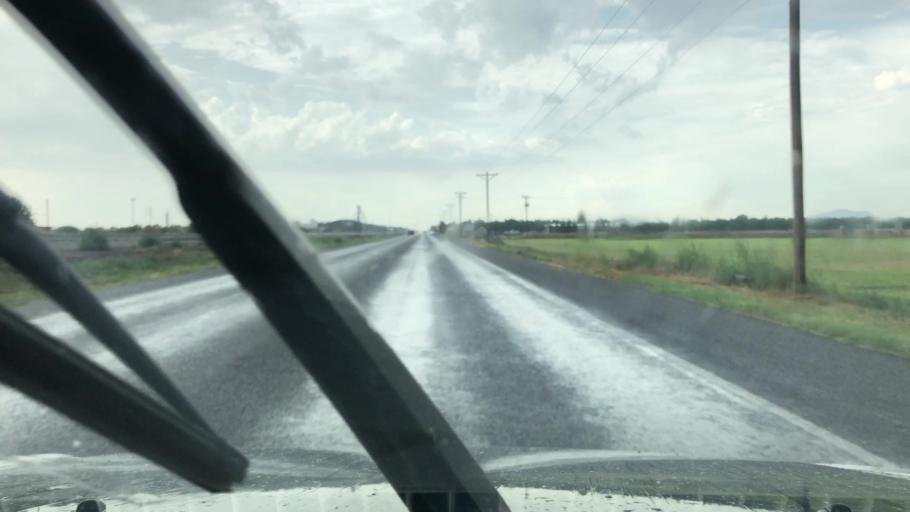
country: US
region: New Mexico
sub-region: Dona Ana County
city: Mesquite
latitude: 32.1562
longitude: -106.6913
